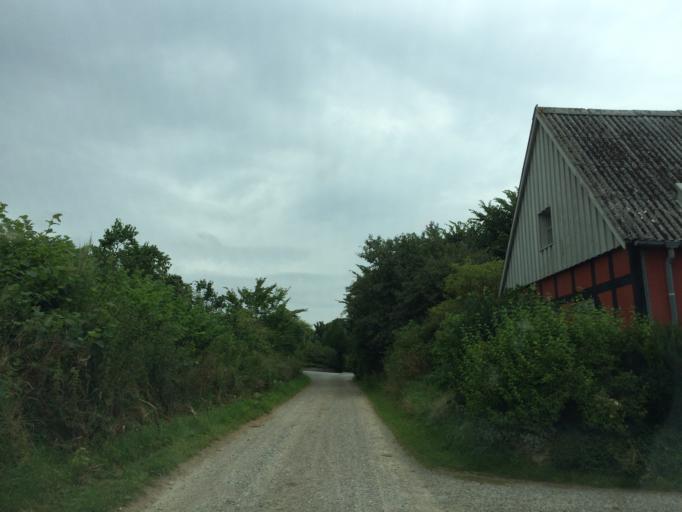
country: DK
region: Central Jutland
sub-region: Syddjurs Kommune
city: Ronde
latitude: 56.2401
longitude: 10.5553
